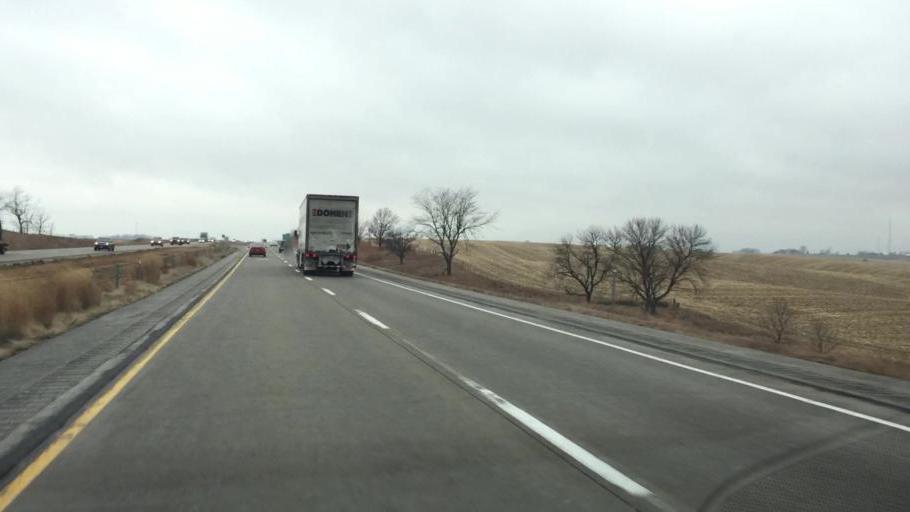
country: US
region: Iowa
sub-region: Iowa County
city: Williamsburg
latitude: 41.6871
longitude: -91.9774
